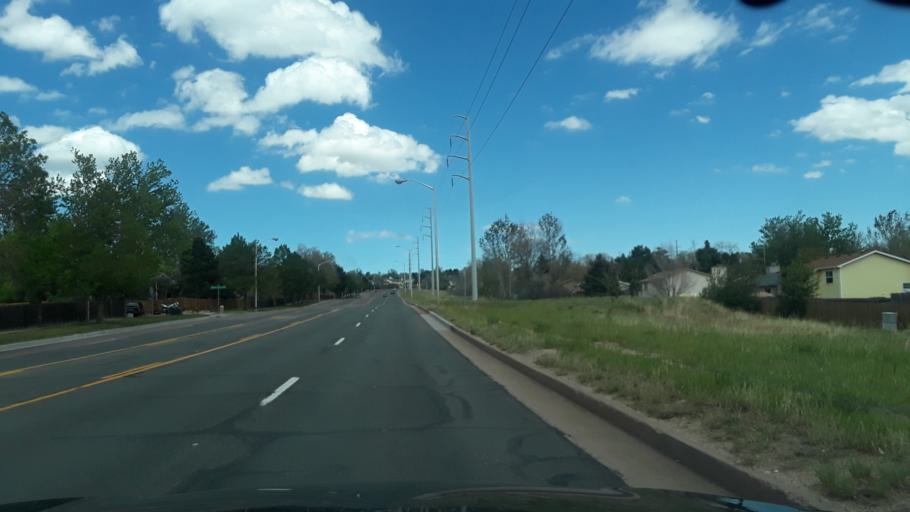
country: US
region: Colorado
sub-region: El Paso County
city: Air Force Academy
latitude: 38.9442
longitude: -104.7903
